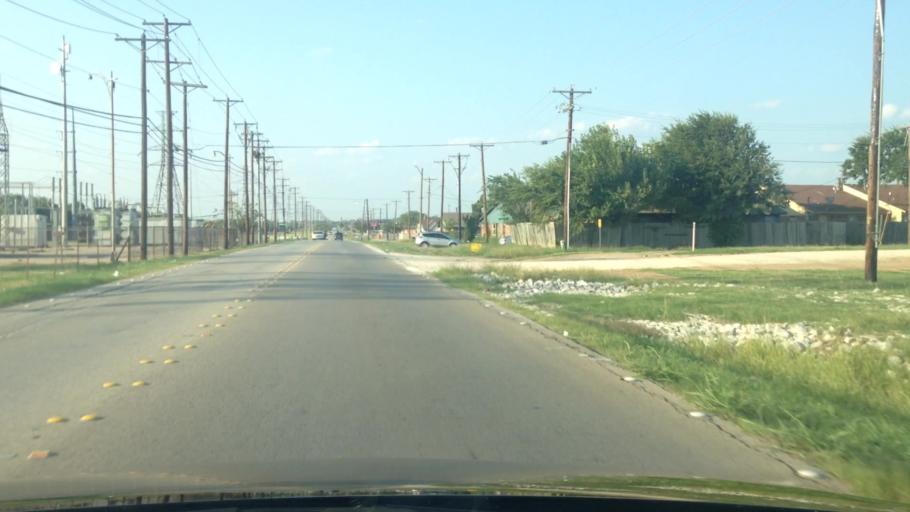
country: US
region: Texas
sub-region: Tarrant County
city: Everman
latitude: 32.6440
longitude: -97.2860
